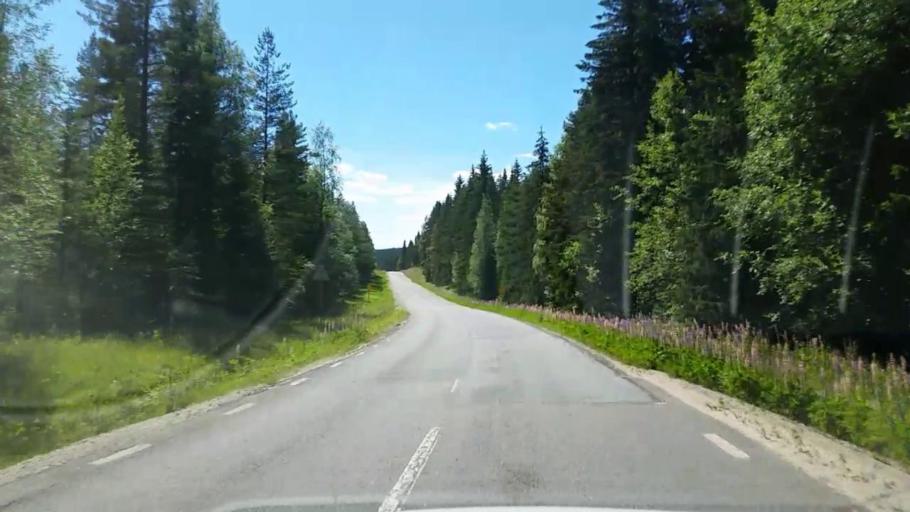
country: SE
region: Gaevleborg
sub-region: Ljusdals Kommun
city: Farila
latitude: 61.6777
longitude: 15.6253
